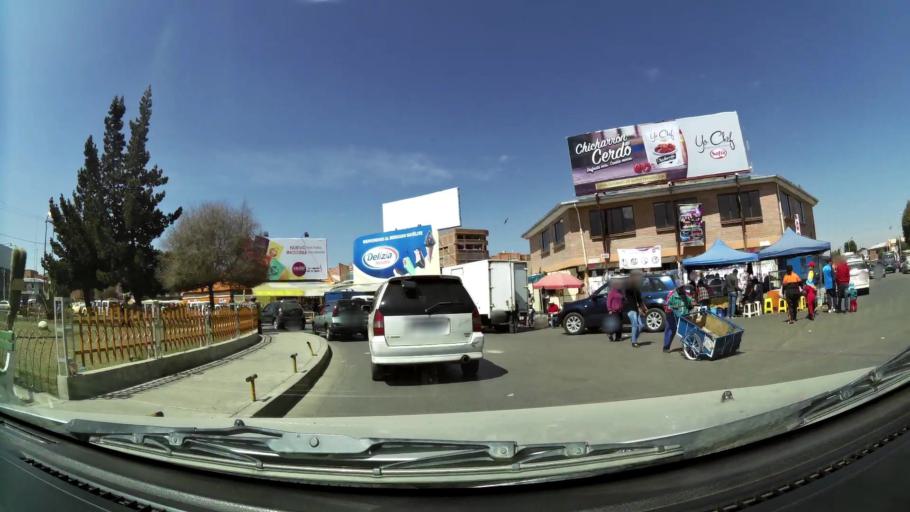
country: BO
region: La Paz
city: La Paz
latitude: -16.5243
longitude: -68.1509
